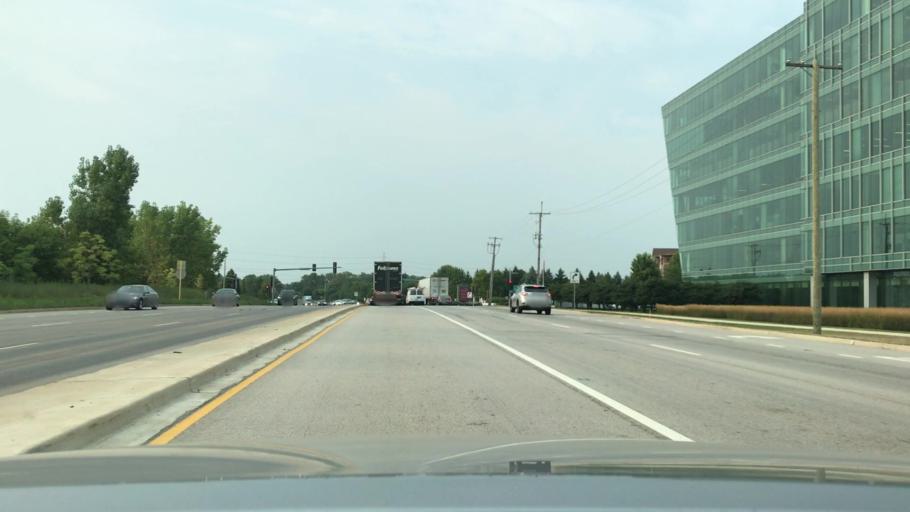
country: US
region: Illinois
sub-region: DuPage County
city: Warrenville
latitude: 41.8082
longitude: -88.2037
